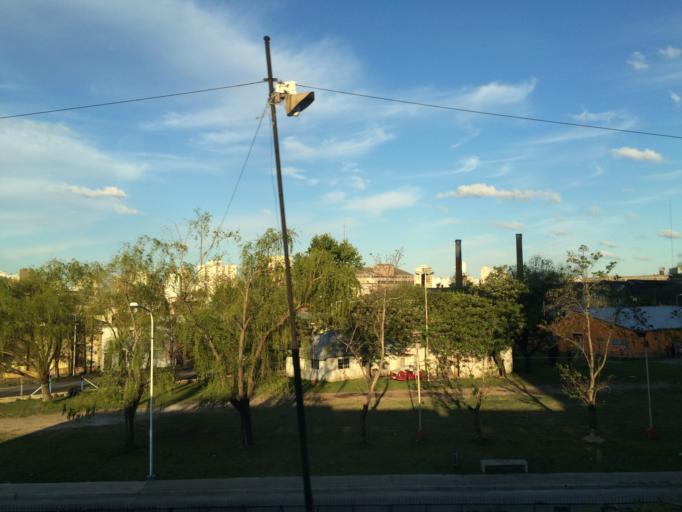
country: AR
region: Buenos Aires
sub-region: Partido de Avellaneda
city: Avellaneda
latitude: -34.6644
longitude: -58.3760
